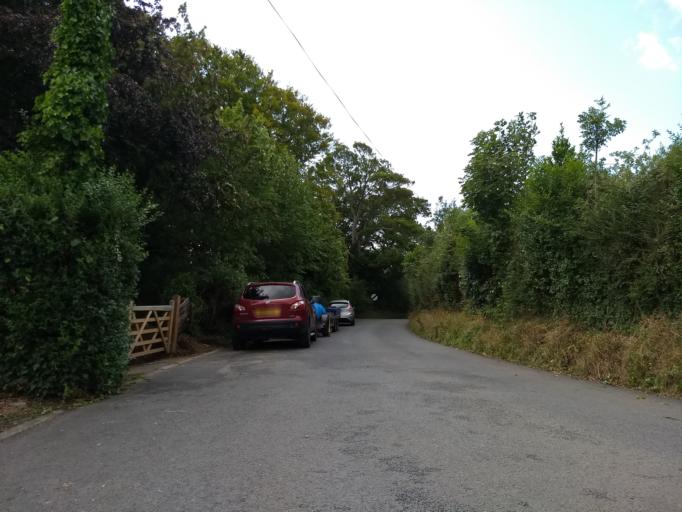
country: GB
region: England
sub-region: Isle of Wight
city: Newport
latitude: 50.6882
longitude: -1.2943
